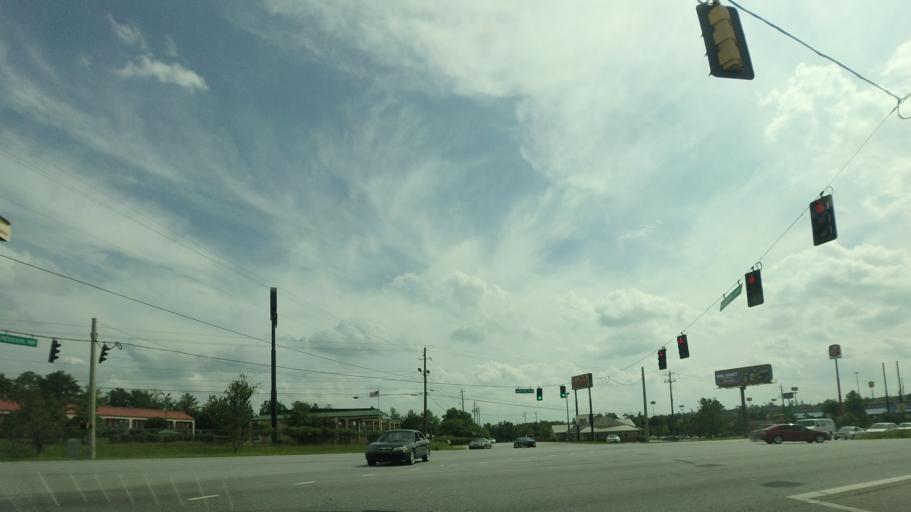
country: US
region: Georgia
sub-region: Bibb County
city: West Point
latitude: 32.8133
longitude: -83.7206
